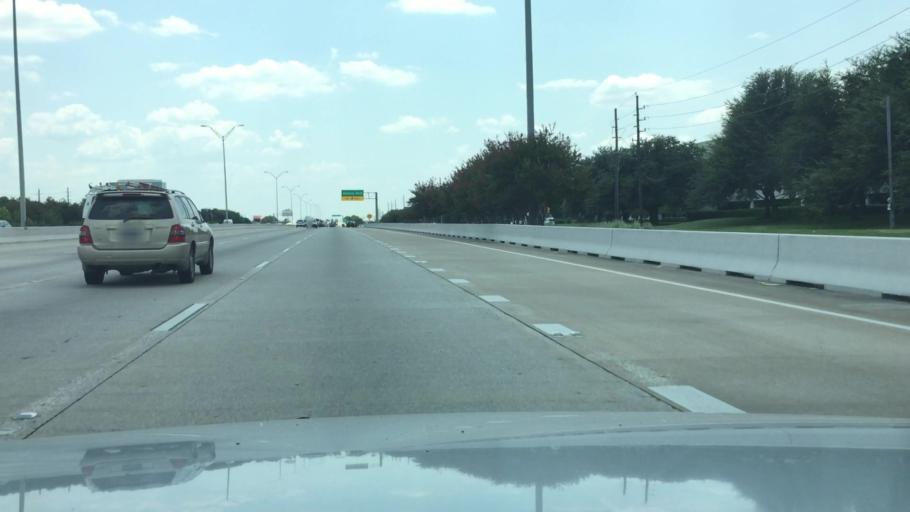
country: US
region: Texas
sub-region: Harris County
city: Bunker Hill Village
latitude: 29.7133
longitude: -95.5576
